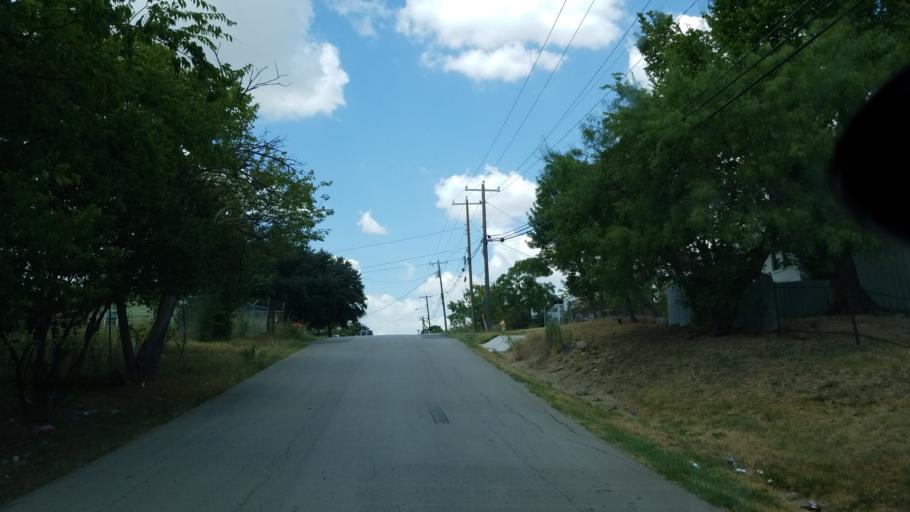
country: US
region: Texas
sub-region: Dallas County
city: Cockrell Hill
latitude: 32.7477
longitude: -96.9127
